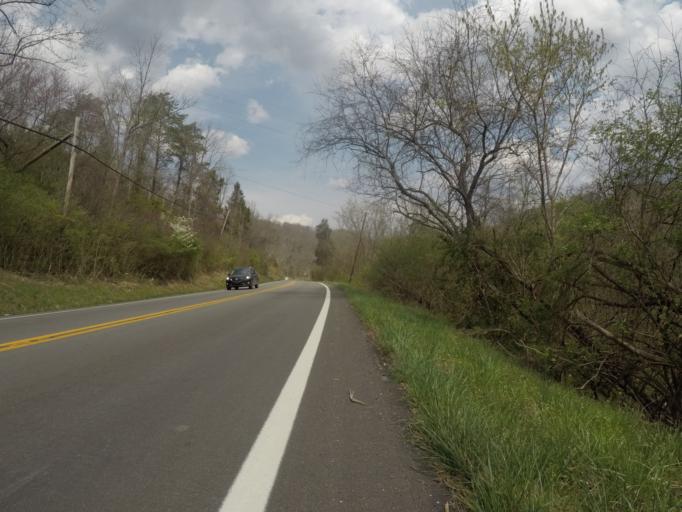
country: US
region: West Virginia
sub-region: Cabell County
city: Pea Ridge
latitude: 38.3917
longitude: -82.3291
